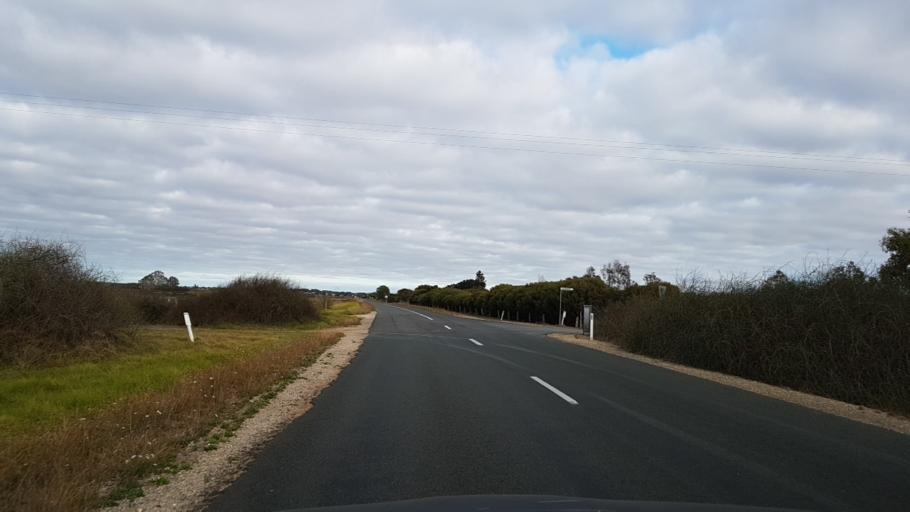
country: AU
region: South Australia
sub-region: Alexandrina
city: Langhorne Creek
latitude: -35.3947
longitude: 139.0046
